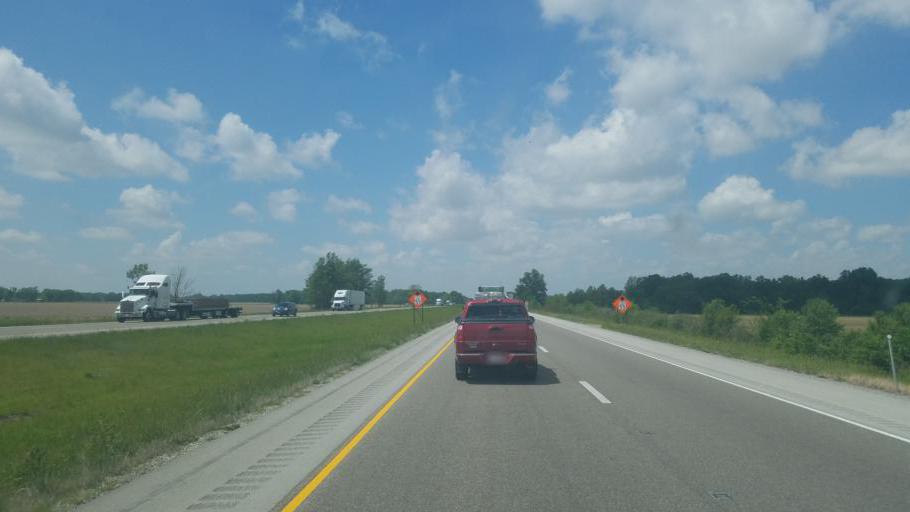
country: US
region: Illinois
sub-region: Cumberland County
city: Toledo
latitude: 39.2276
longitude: -88.2227
